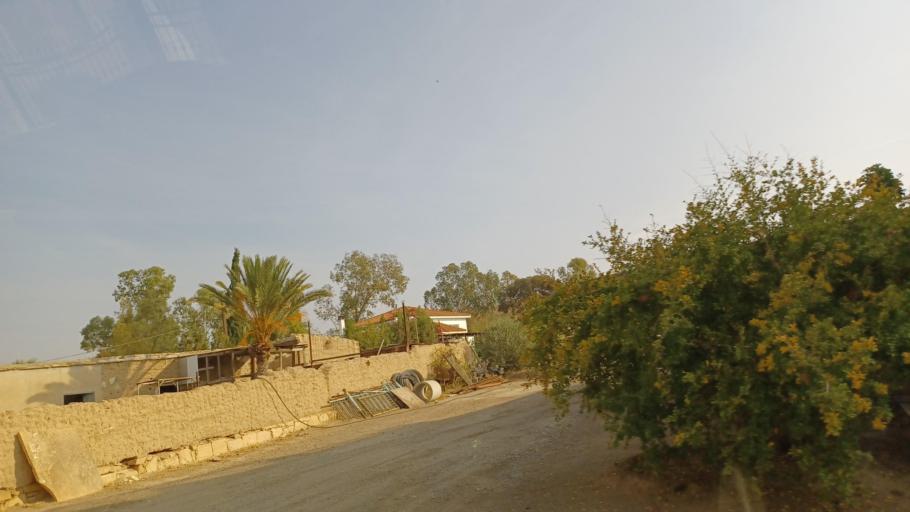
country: CY
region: Larnaka
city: Troulloi
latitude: 35.0306
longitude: 33.6157
